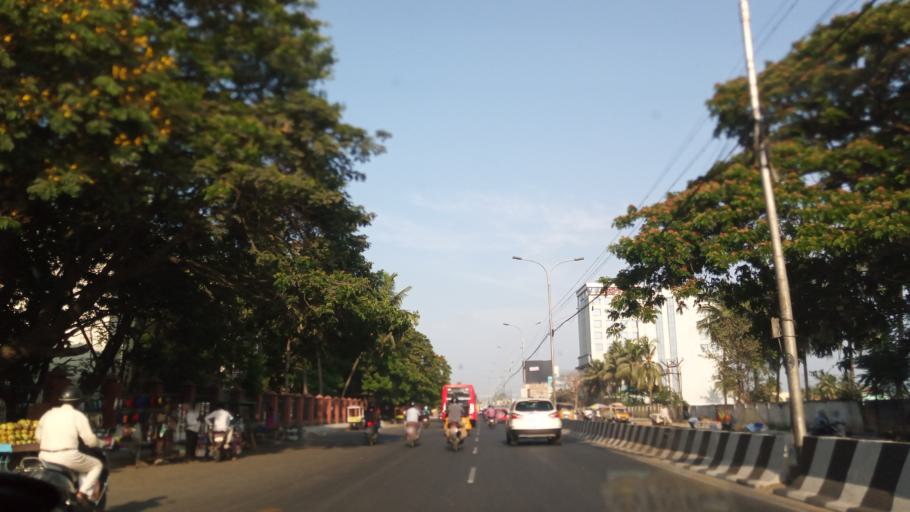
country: IN
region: Tamil Nadu
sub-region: Thiruvallur
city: Porur
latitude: 13.0366
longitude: 80.1436
